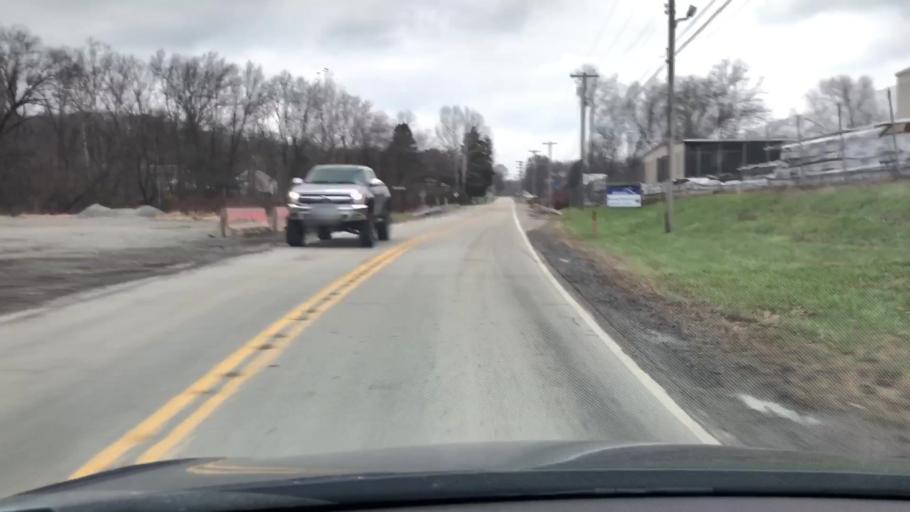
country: US
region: Pennsylvania
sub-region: Westmoreland County
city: New Stanton
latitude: 40.2064
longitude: -79.6215
